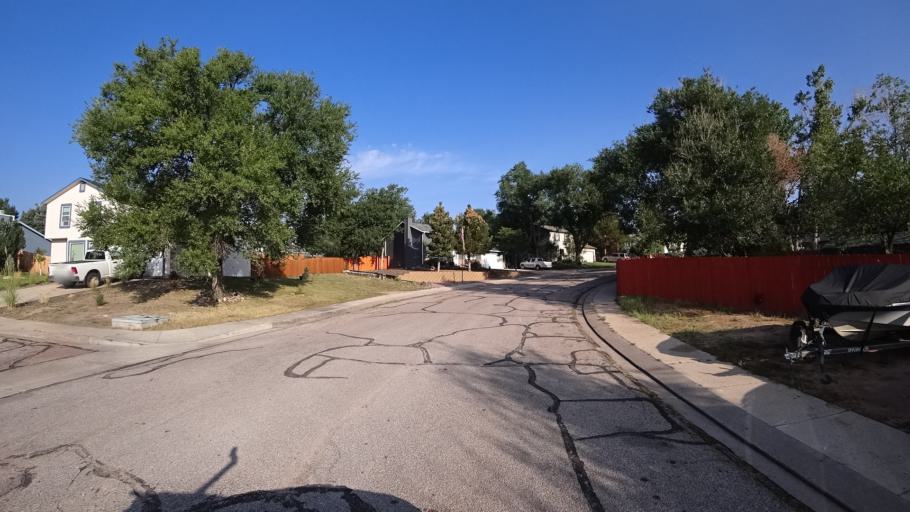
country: US
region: Colorado
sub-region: El Paso County
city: Colorado Springs
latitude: 38.8837
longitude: -104.7927
